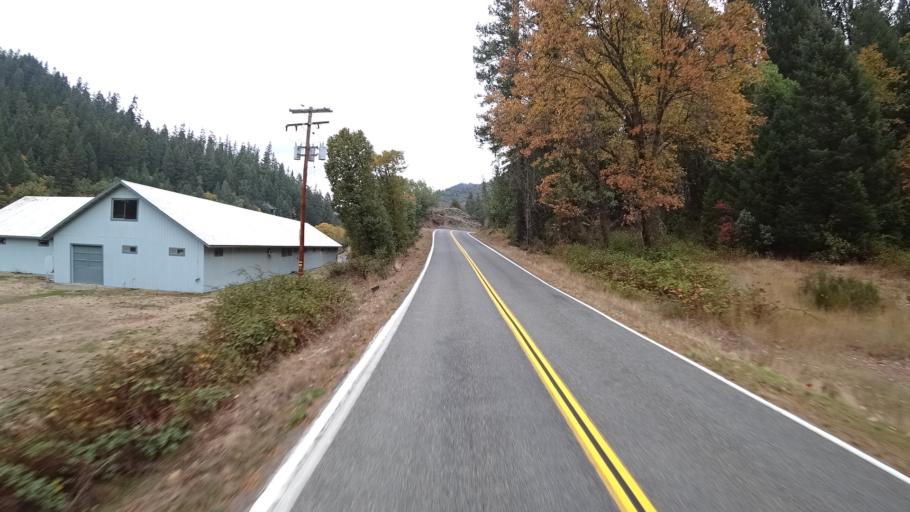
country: US
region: California
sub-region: Siskiyou County
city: Happy Camp
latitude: 41.8402
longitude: -123.3838
